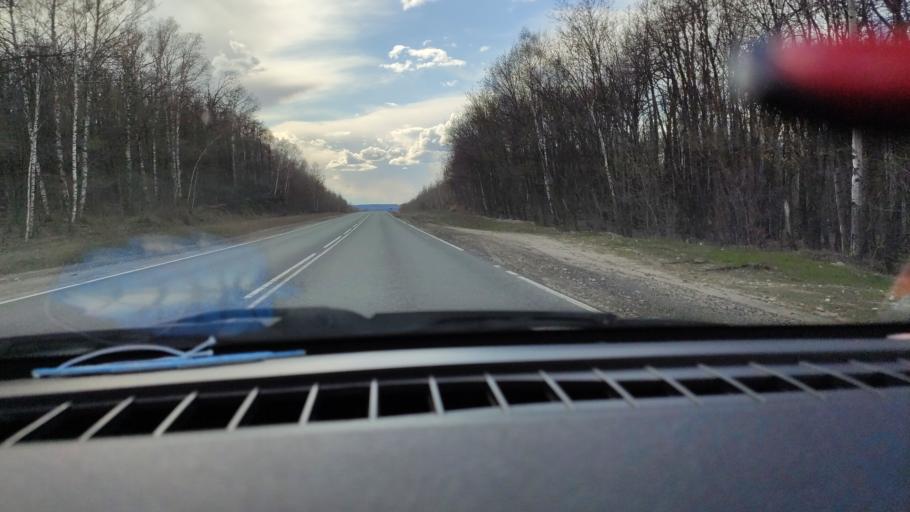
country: RU
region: Saratov
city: Vol'sk
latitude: 52.1122
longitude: 47.3228
